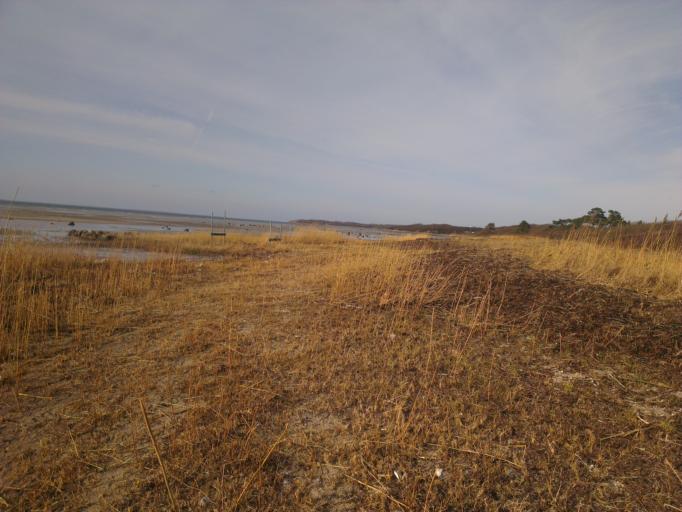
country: DK
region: Capital Region
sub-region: Frederikssund Kommune
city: Jaegerspris
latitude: 55.8549
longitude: 11.9578
